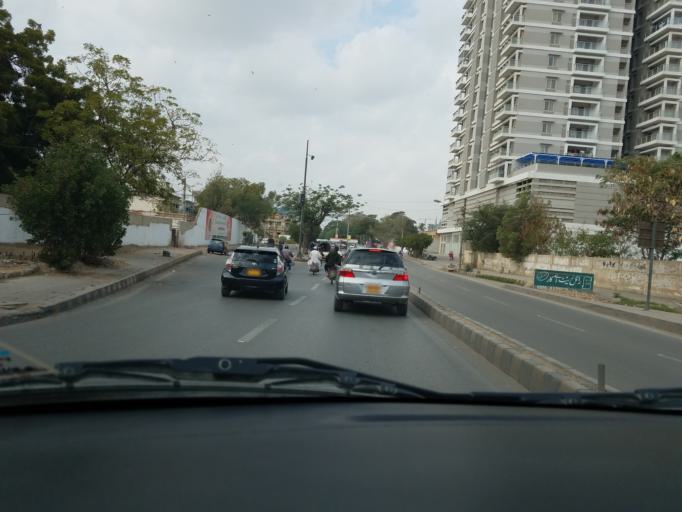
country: PK
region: Sindh
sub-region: Karachi District
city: Karachi
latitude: 24.8422
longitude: 67.0325
